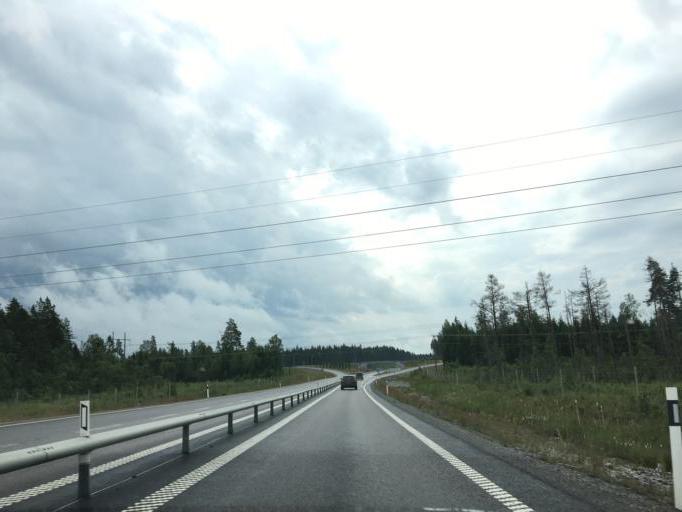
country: SE
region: Soedermanland
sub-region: Katrineholms Kommun
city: Katrineholm
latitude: 58.9971
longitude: 16.2559
